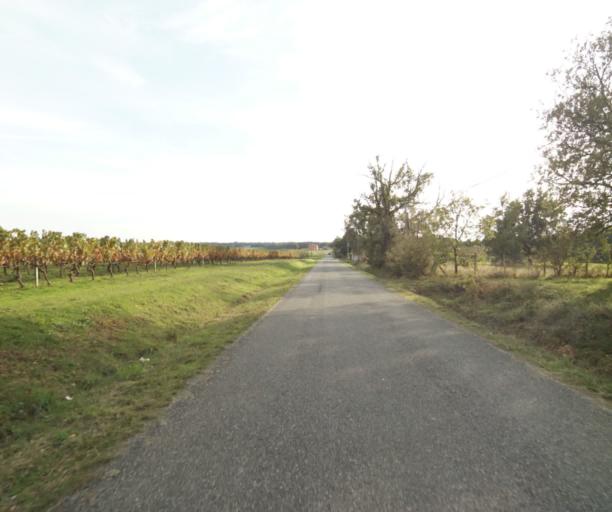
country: FR
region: Midi-Pyrenees
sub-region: Departement du Tarn-et-Garonne
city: Campsas
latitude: 43.8895
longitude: 1.3257
